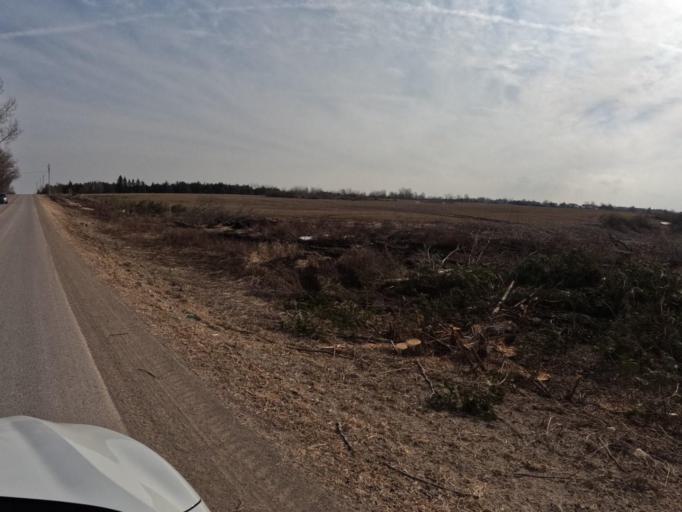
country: CA
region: Ontario
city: Orangeville
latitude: 43.8934
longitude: -80.2663
